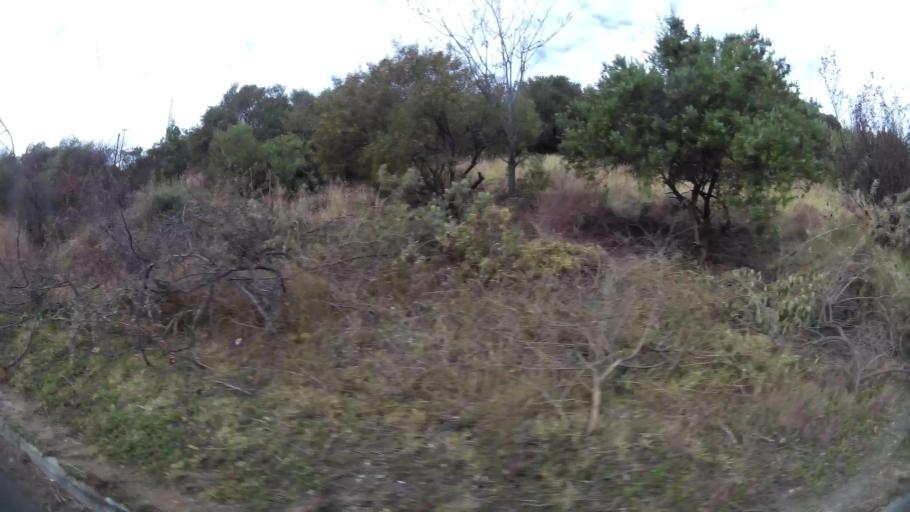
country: ZA
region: Orange Free State
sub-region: Mangaung Metropolitan Municipality
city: Bloemfontein
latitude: -29.1003
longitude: 26.2126
